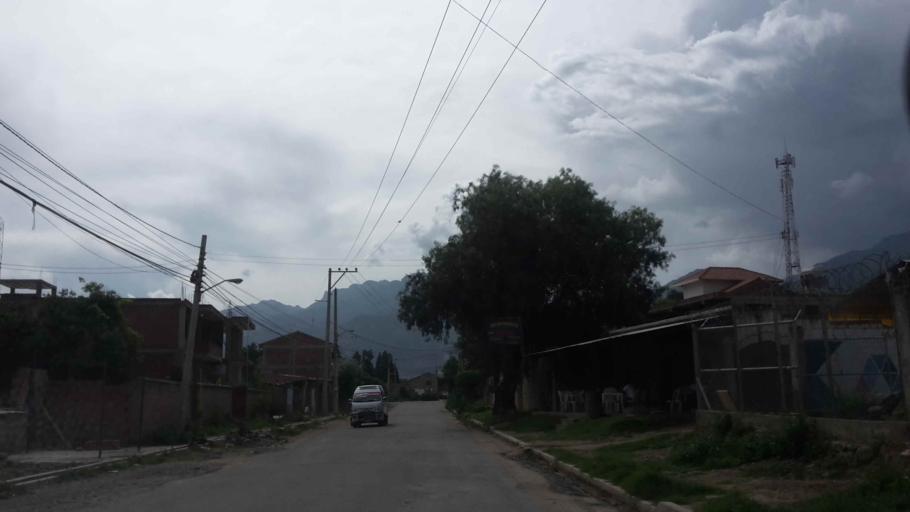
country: BO
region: Cochabamba
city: Cochabamba
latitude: -17.3347
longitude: -66.2344
